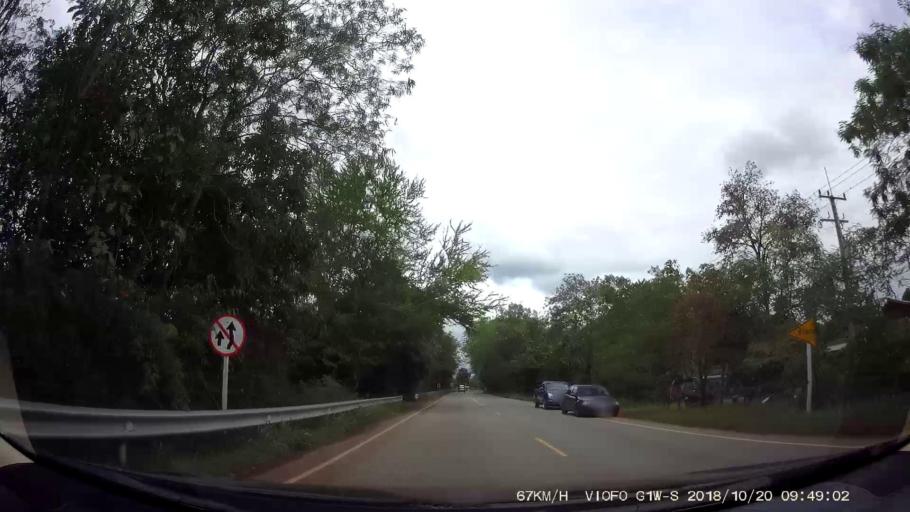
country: TH
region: Chaiyaphum
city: Khon San
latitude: 16.5159
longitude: 101.9075
